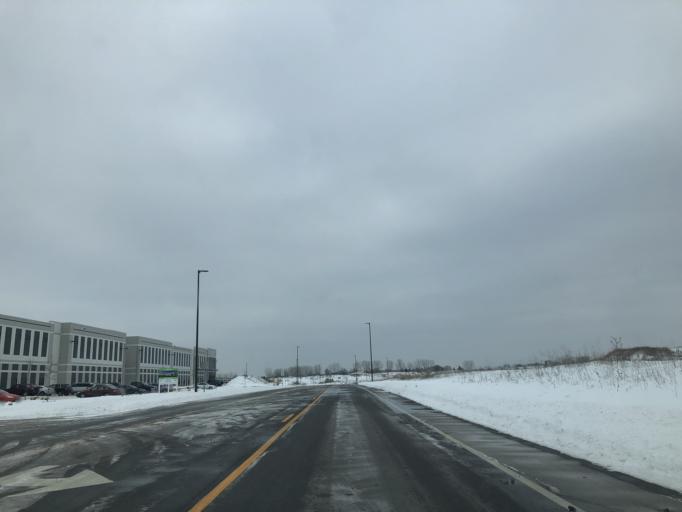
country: US
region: Minnesota
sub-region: Hennepin County
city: Osseo
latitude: 45.0919
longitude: -93.4153
